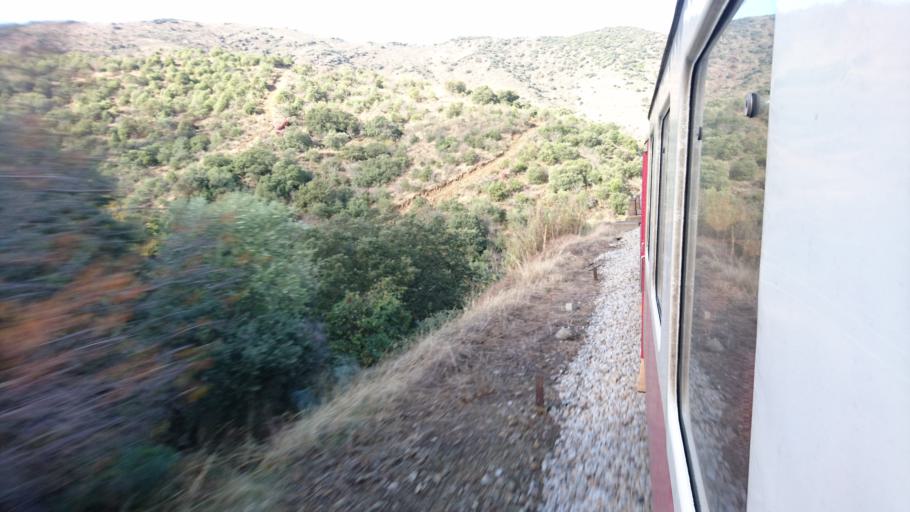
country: PT
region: Guarda
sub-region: Vila Nova de Foz Coa
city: Vila Nova de Foz Coa
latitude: 41.1243
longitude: -7.1903
